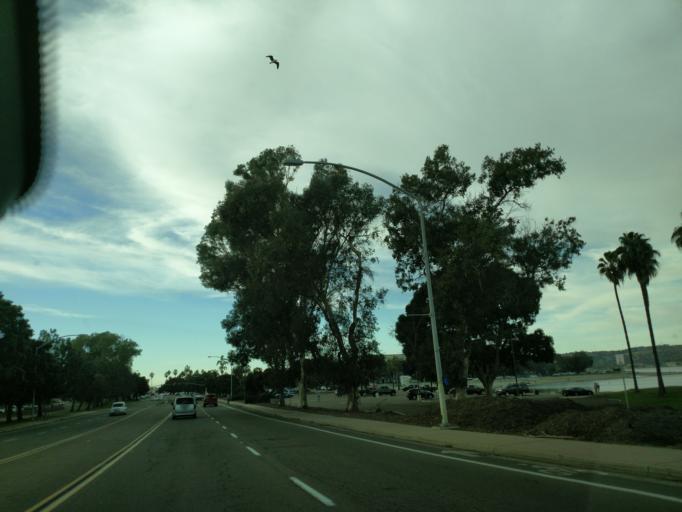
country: US
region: California
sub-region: San Diego County
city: La Jolla
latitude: 32.7694
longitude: -117.2444
